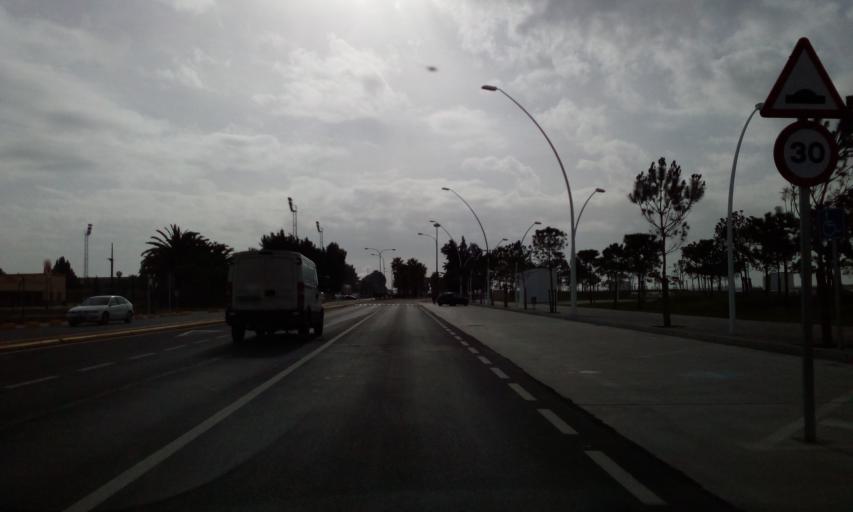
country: ES
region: Andalusia
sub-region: Provincia de Huelva
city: Huelva
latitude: 37.2441
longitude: -6.9552
